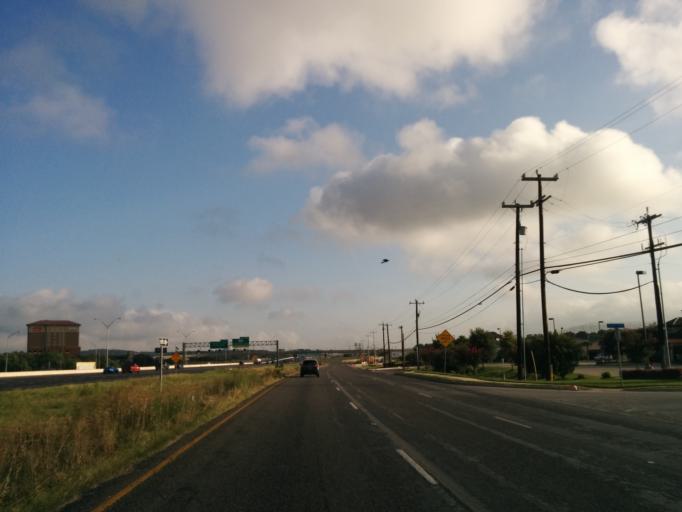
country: US
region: Texas
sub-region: Bexar County
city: Shavano Park
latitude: 29.5840
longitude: -98.5969
